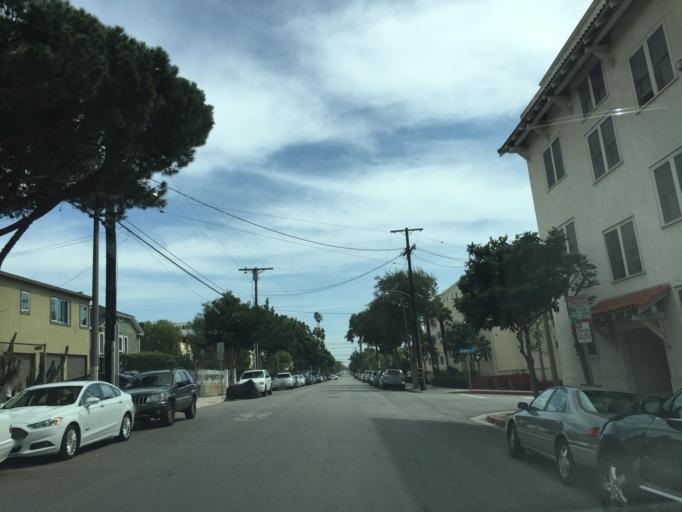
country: US
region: California
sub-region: Los Angeles County
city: Santa Monica
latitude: 34.0054
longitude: -118.4846
